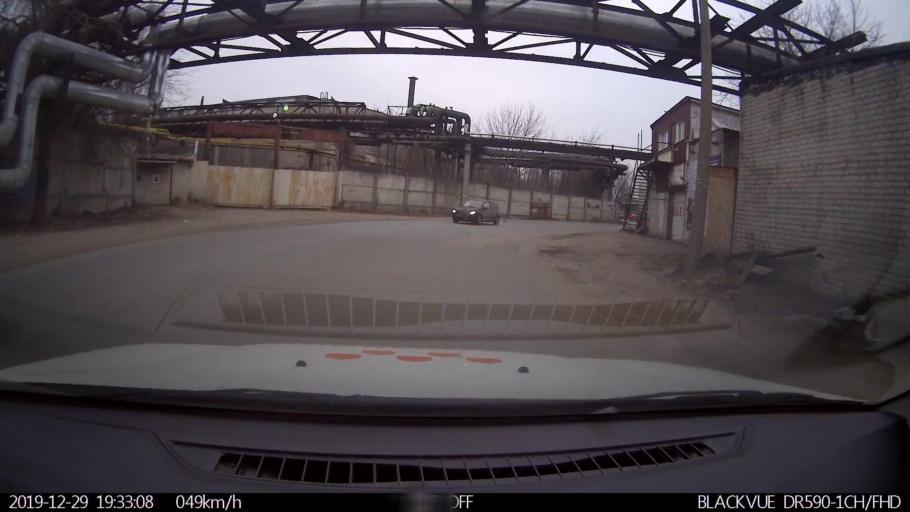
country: RU
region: Nizjnij Novgorod
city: Neklyudovo
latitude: 56.3532
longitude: 43.8786
